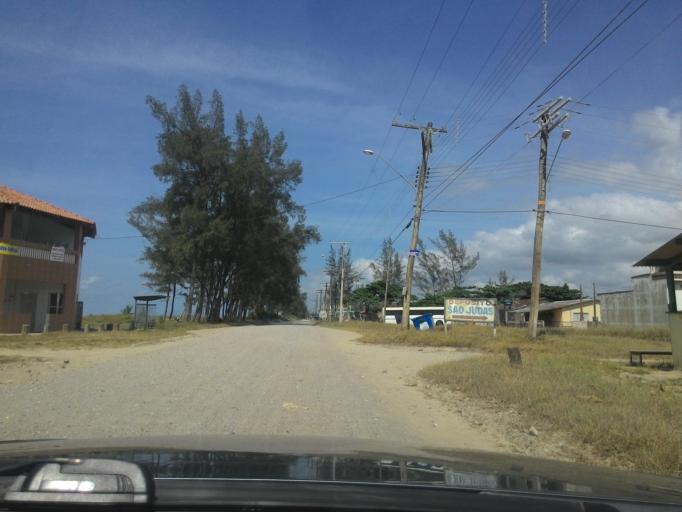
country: BR
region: Sao Paulo
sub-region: Iguape
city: Iguape
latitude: -24.8433
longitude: -47.6852
